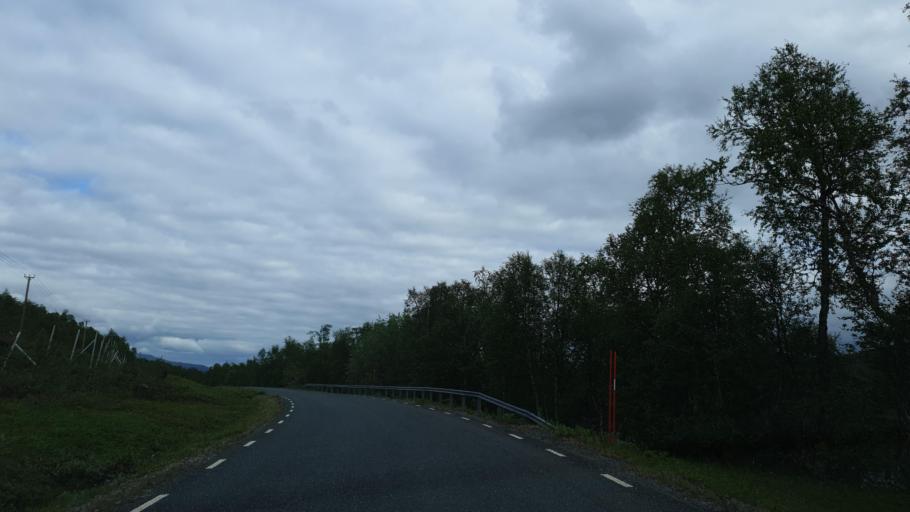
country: NO
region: Nordland
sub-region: Hattfjelldal
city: Hattfjelldal
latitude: 65.4164
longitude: 14.7229
